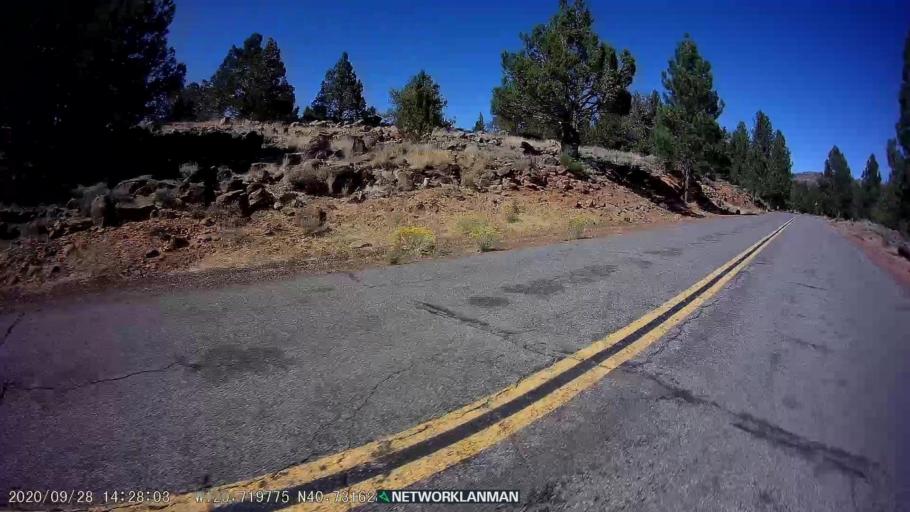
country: US
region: California
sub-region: Lassen County
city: Susanville
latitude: 40.7319
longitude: -120.7197
